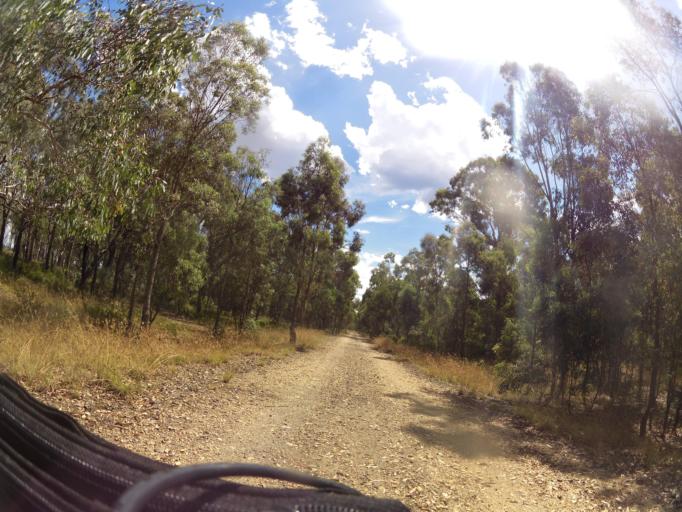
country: AU
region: Victoria
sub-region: Wellington
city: Heyfield
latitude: -37.9827
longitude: 146.7287
